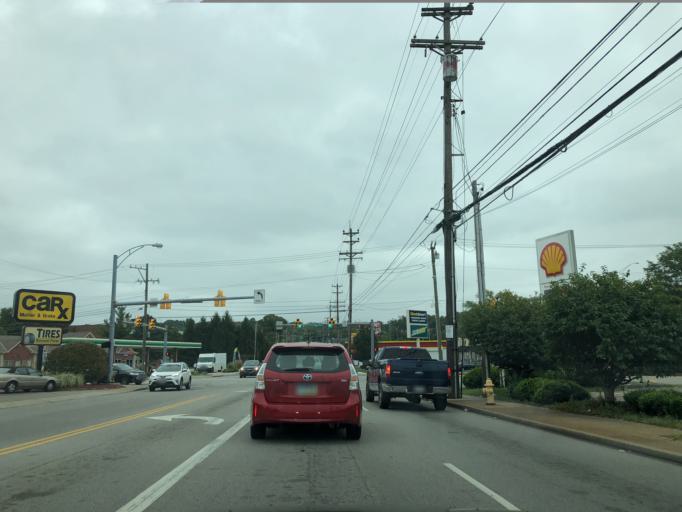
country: US
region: Ohio
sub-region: Hamilton County
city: Reading
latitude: 39.2115
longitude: -84.4484
